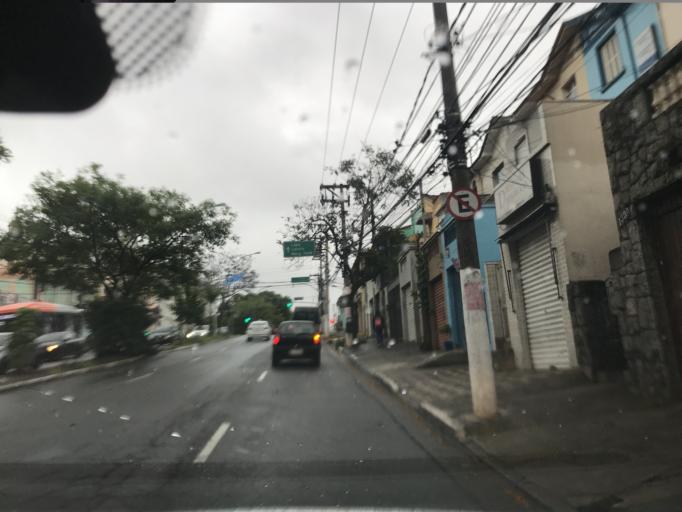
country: BR
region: Sao Paulo
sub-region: Sao Paulo
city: Sao Paulo
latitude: -23.5358
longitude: -46.6889
